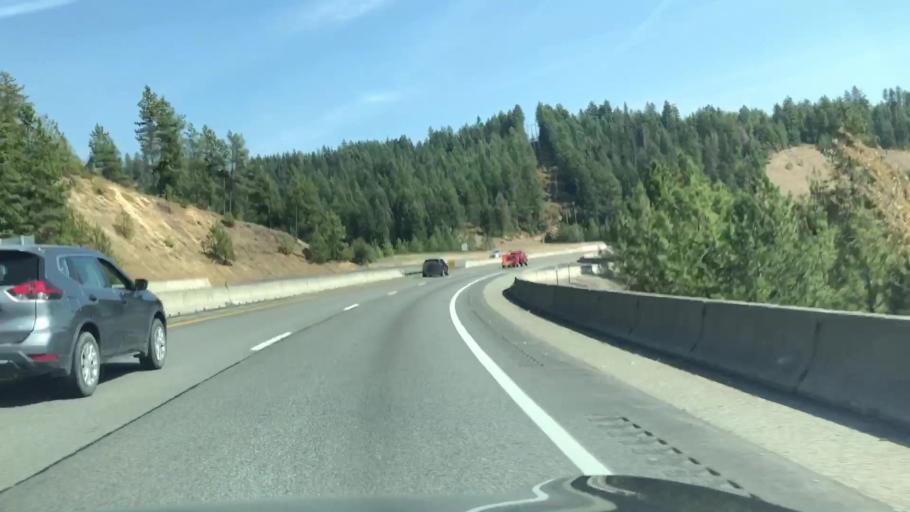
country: US
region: Idaho
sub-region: Kootenai County
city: Coeur d'Alene
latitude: 47.6628
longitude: -116.7324
